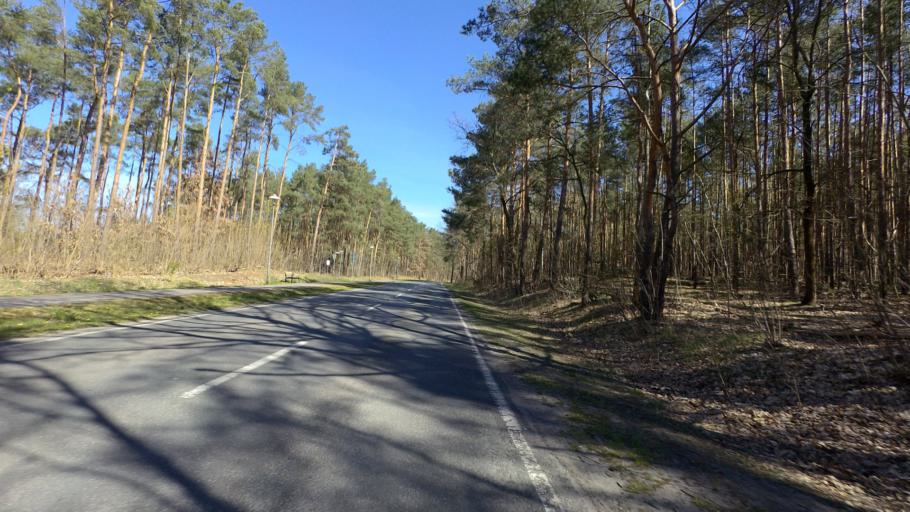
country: DE
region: Brandenburg
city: Zeuthen
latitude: 52.3421
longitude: 13.6174
